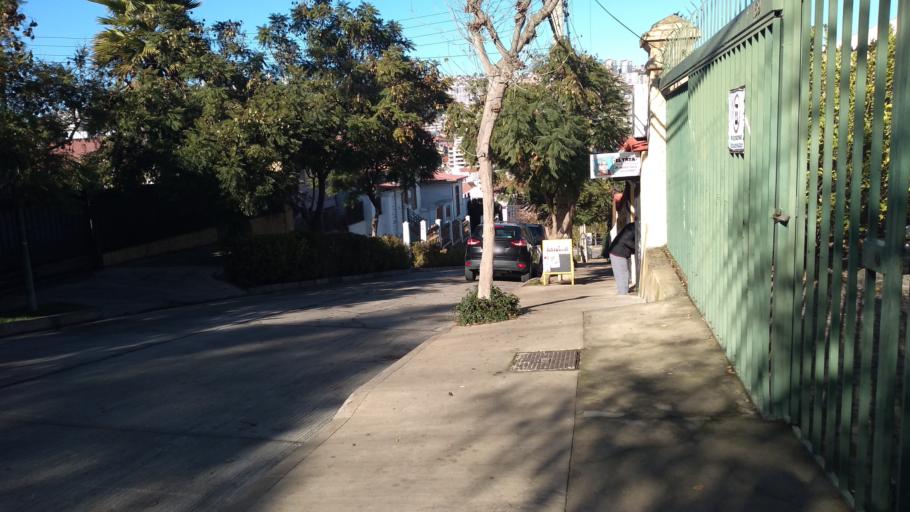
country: CL
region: Valparaiso
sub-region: Provincia de Valparaiso
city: Vina del Mar
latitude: -33.0228
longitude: -71.5631
